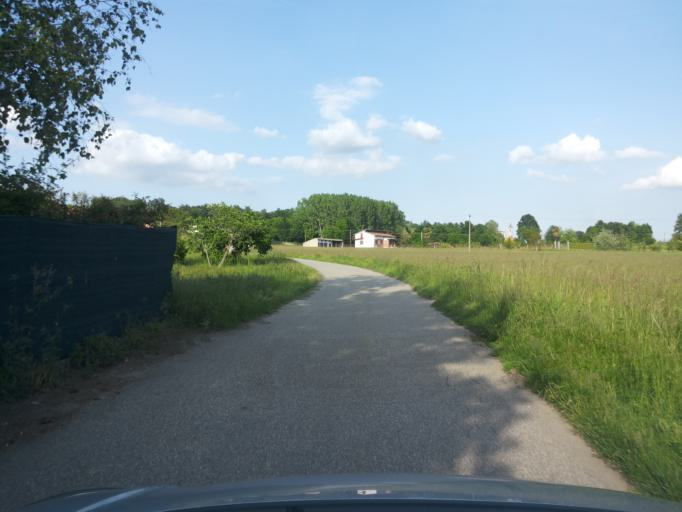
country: IT
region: Piedmont
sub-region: Provincia di Torino
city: Azeglio
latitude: 45.4246
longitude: 7.9807
